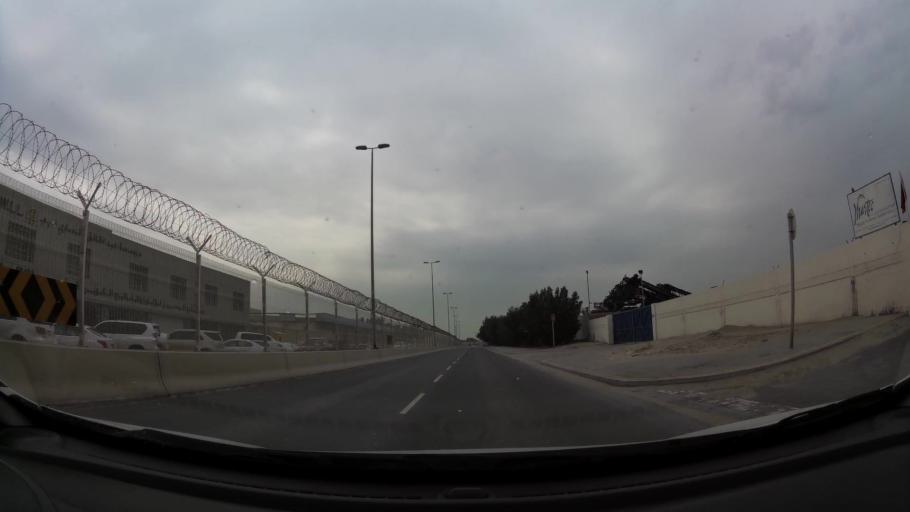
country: BH
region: Northern
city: Sitrah
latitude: 26.1798
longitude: 50.6056
